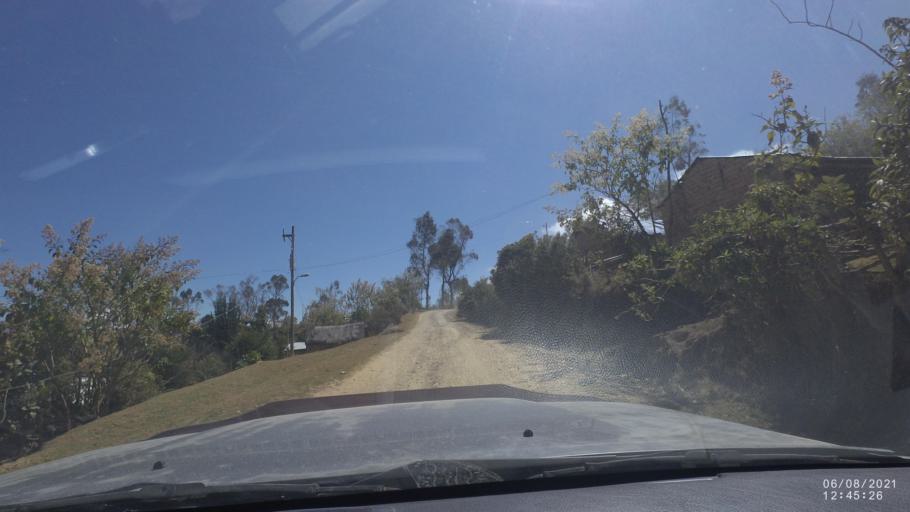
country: BO
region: Cochabamba
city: Colchani
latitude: -16.7654
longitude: -66.6641
